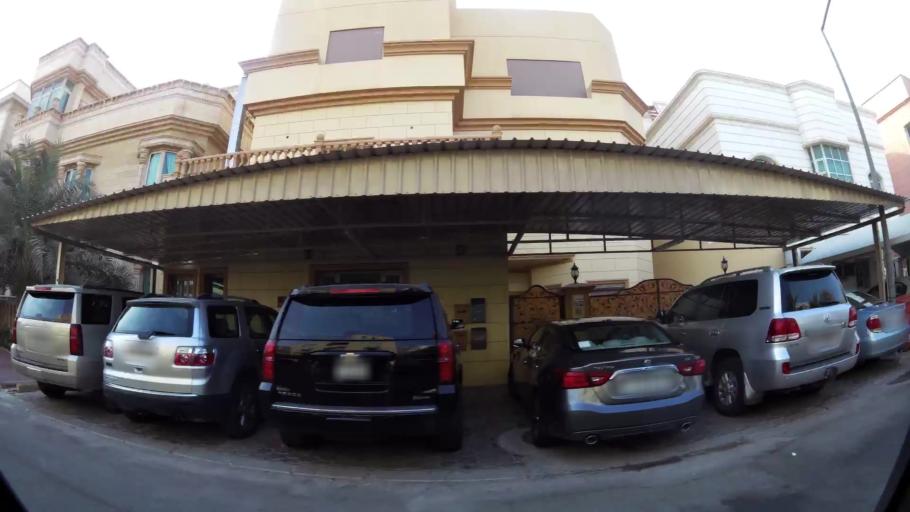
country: KW
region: Muhafazat Hawalli
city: Hawalli
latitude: 29.3202
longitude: 48.0011
